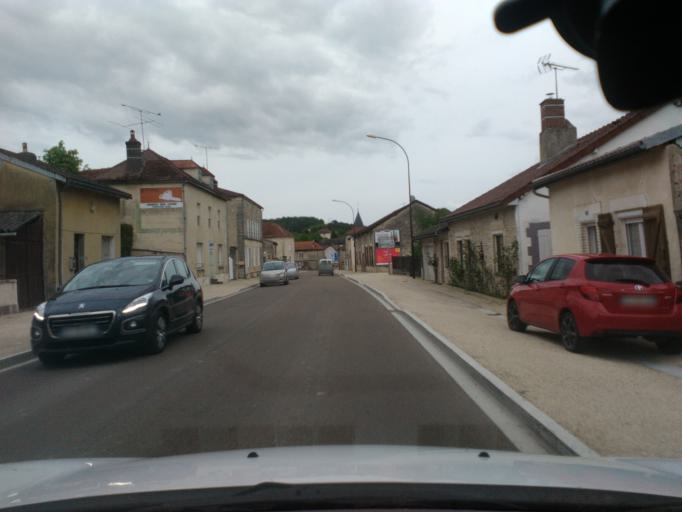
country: FR
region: Champagne-Ardenne
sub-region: Departement de l'Aube
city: Bar-sur-Aube
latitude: 48.2691
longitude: 4.6456
